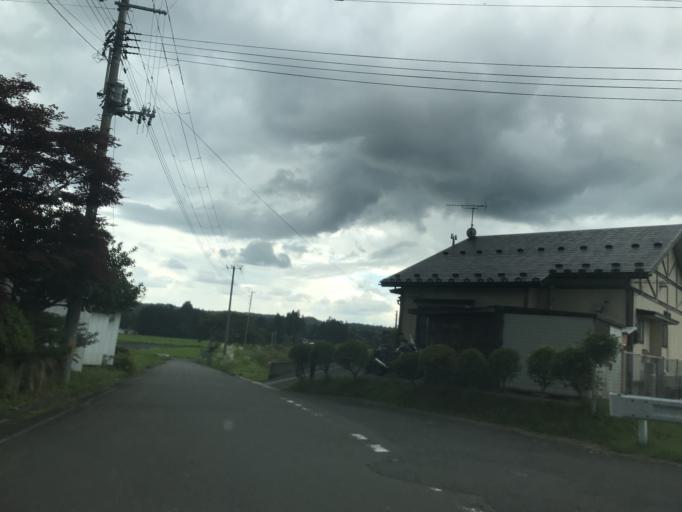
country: JP
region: Iwate
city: Ichinoseki
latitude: 38.9525
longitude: 141.0475
